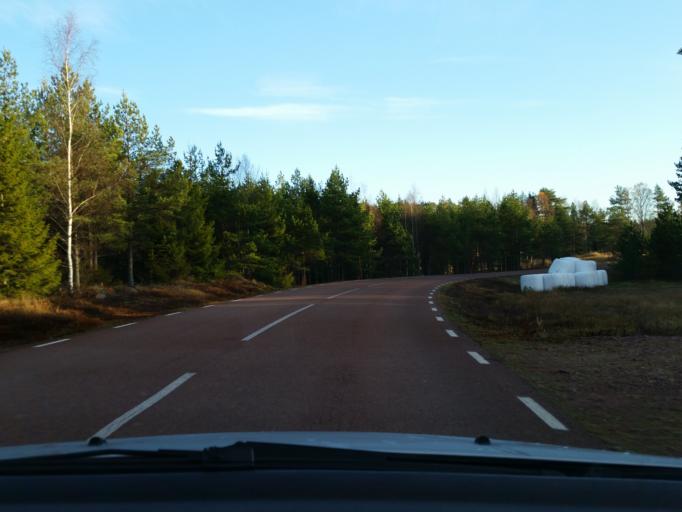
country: AX
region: Alands landsbygd
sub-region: Sund
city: Sund
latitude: 60.2809
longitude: 20.1089
